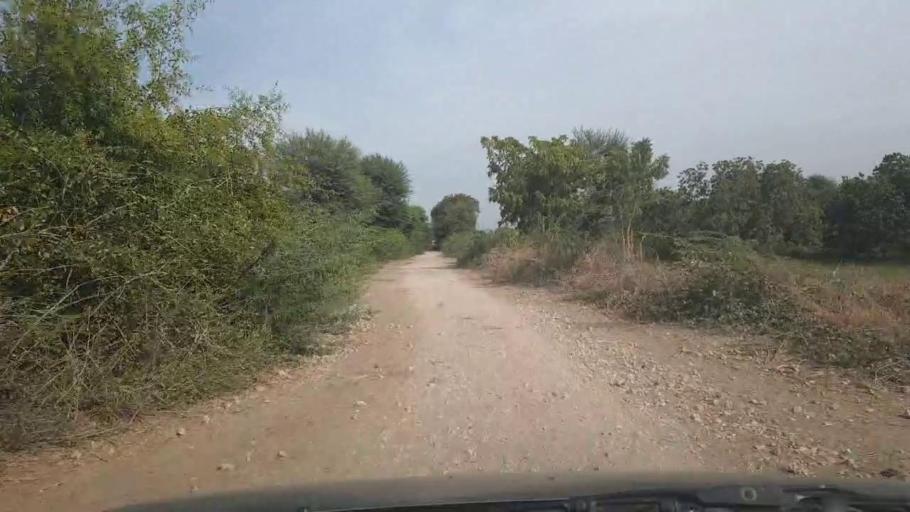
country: PK
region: Sindh
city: Kunri
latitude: 25.2934
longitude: 69.5855
